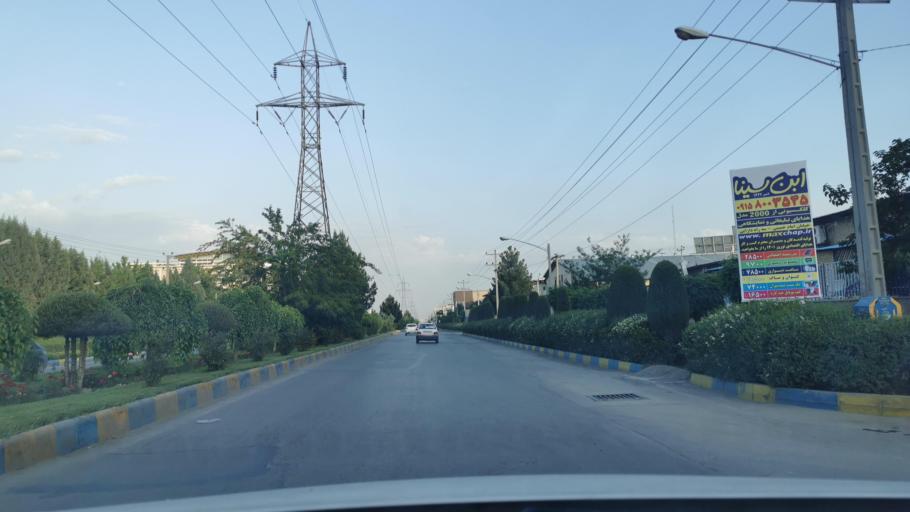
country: IR
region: Razavi Khorasan
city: Torqabeh
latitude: 36.4283
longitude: 59.4201
